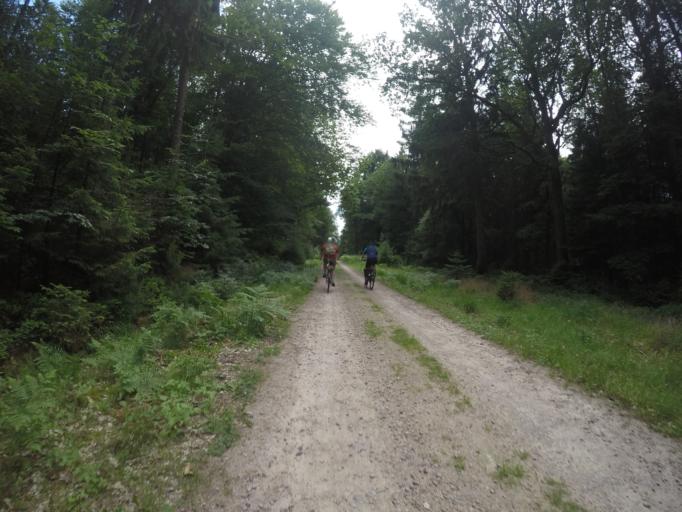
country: DE
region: Lower Saxony
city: Undeloh
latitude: 53.2375
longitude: 9.9626
